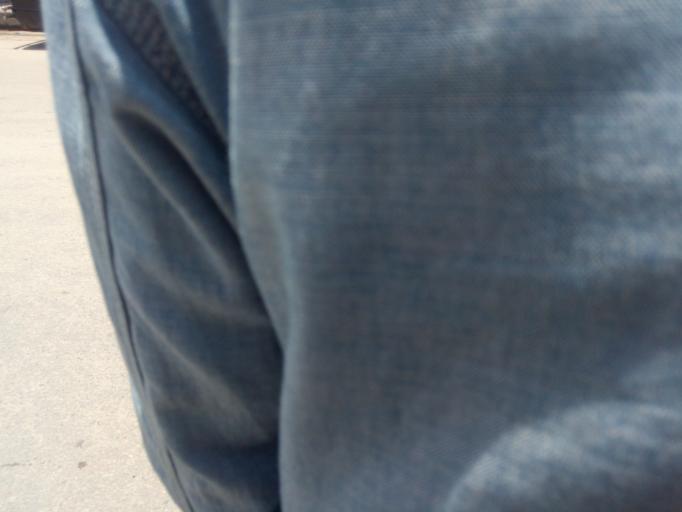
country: BD
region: Dhaka
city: Paltan
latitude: 23.7588
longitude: 90.4415
